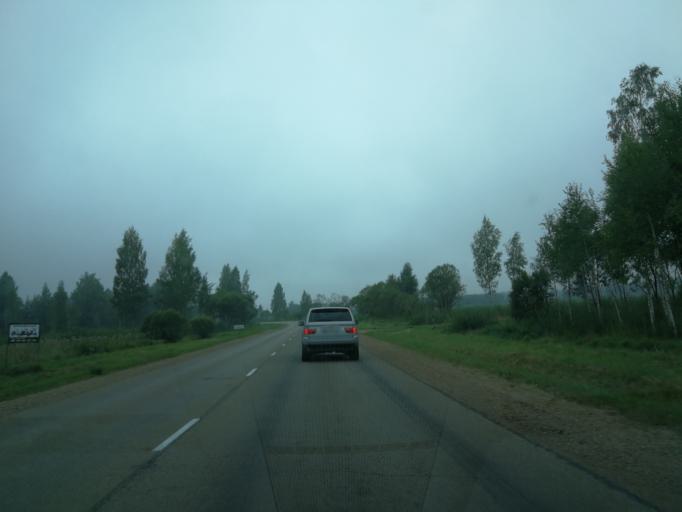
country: LV
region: Preilu Rajons
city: Preili
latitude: 56.3014
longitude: 26.7249
